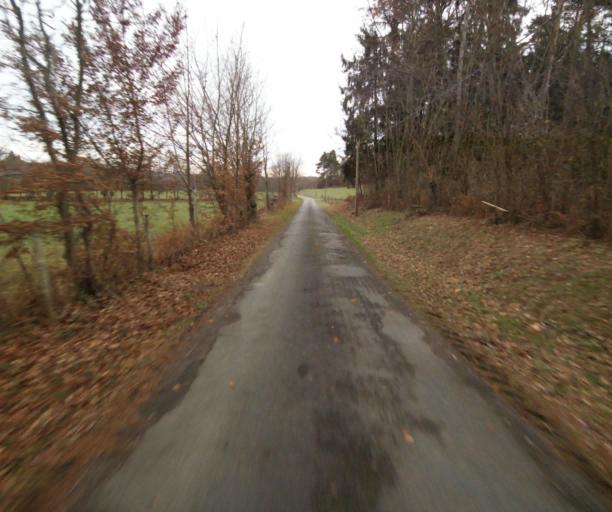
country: FR
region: Limousin
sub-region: Departement de la Correze
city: Chameyrat
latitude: 45.2321
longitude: 1.6719
